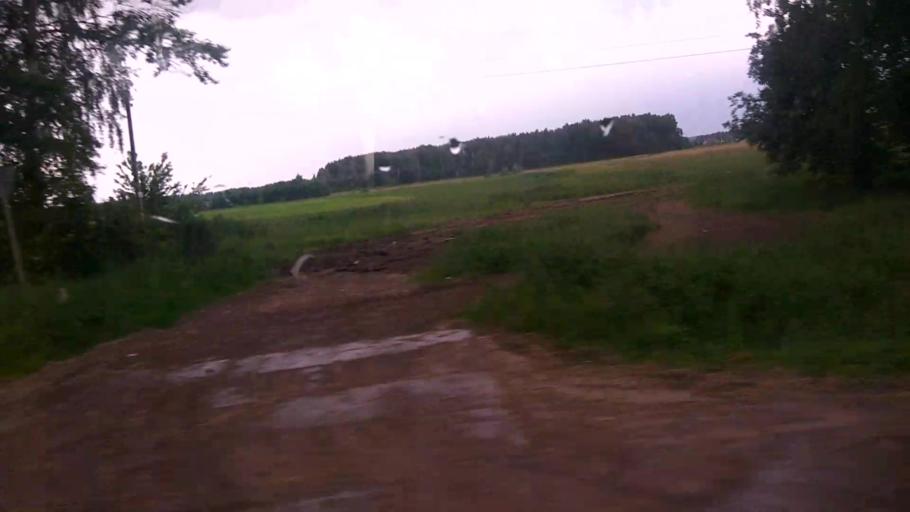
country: RU
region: Moskovskaya
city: Zaraysk
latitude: 54.7692
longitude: 38.8260
